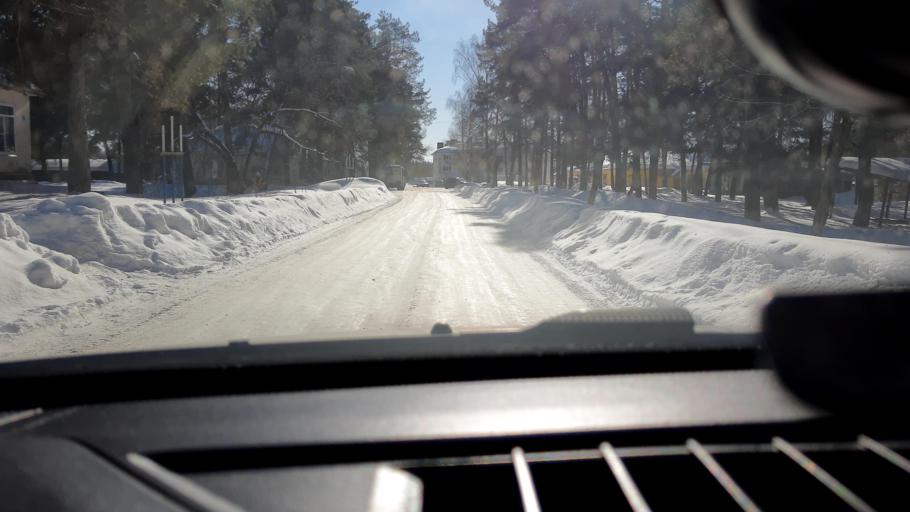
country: RU
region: Nizjnij Novgorod
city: Yuganets
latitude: 56.2469
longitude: 43.2321
